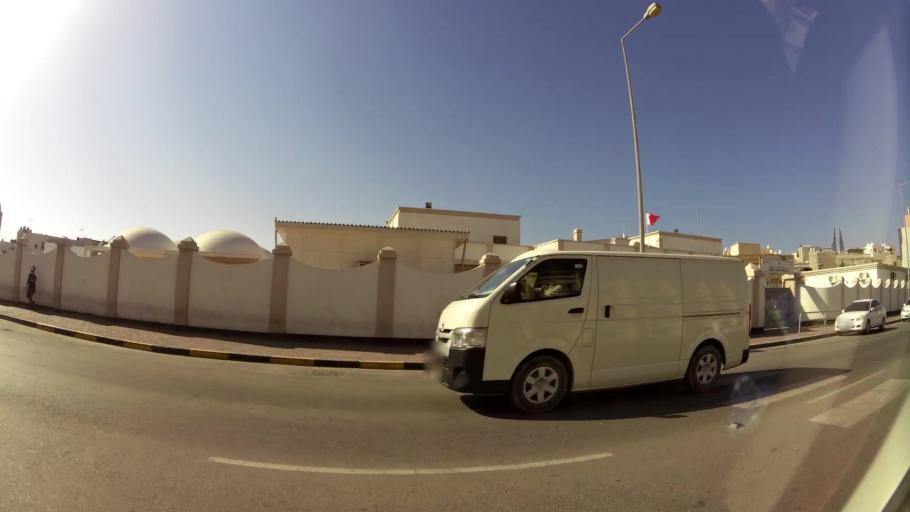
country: BH
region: Manama
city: Manama
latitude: 26.2262
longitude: 50.5783
